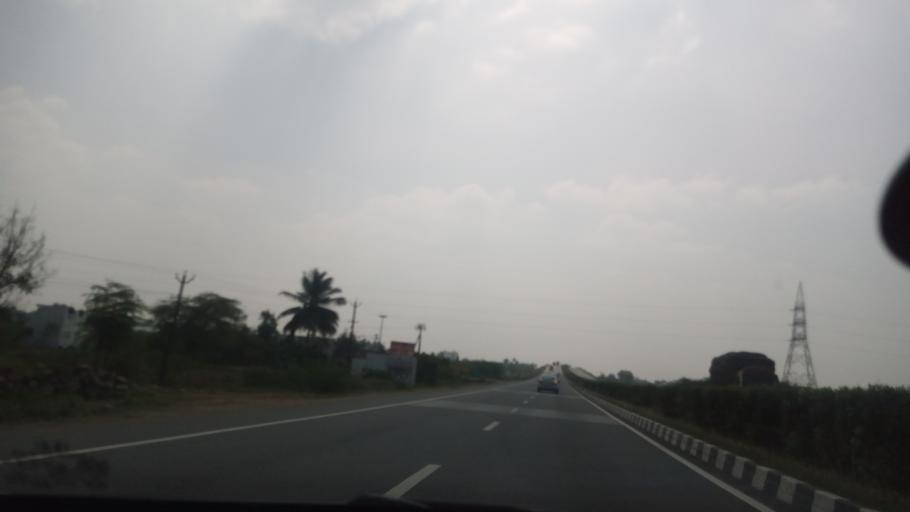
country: IN
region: Tamil Nadu
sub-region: Dharmapuri
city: Dharmapuri
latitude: 12.1556
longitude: 78.1511
